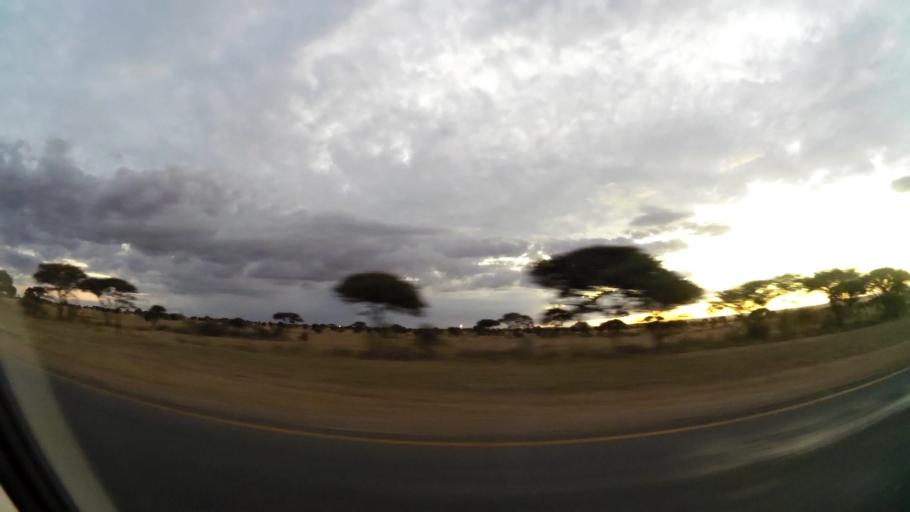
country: ZA
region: Limpopo
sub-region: Capricorn District Municipality
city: Polokwane
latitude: -23.8336
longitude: 29.4264
